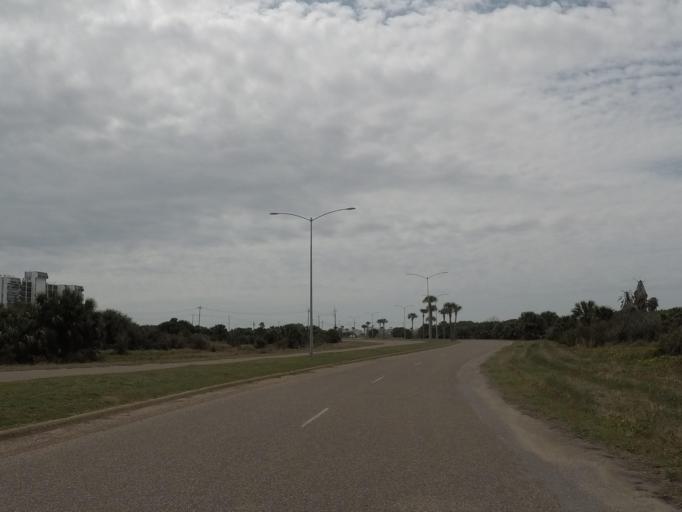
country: US
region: Texas
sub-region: Galveston County
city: Galveston
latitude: 29.3177
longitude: -94.7564
